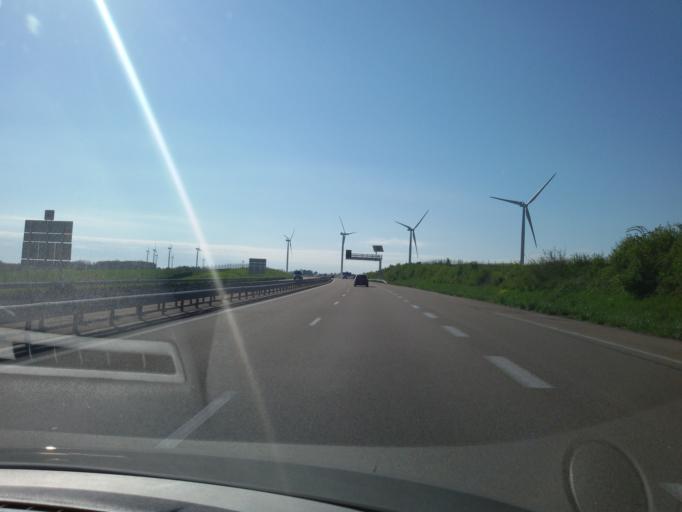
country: FR
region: Bourgogne
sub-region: Departement de l'Yonne
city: Venoy
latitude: 47.7848
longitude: 3.6762
